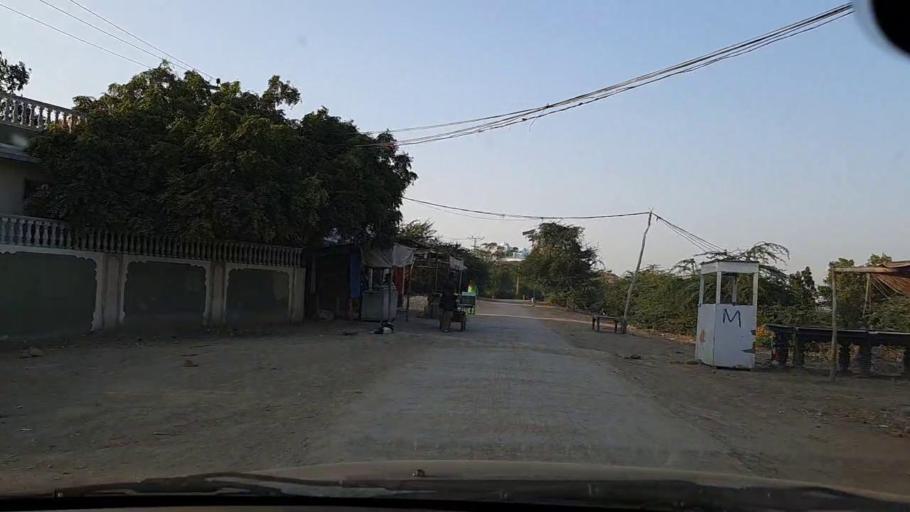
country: PK
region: Sindh
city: Thatta
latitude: 24.5584
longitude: 67.8813
